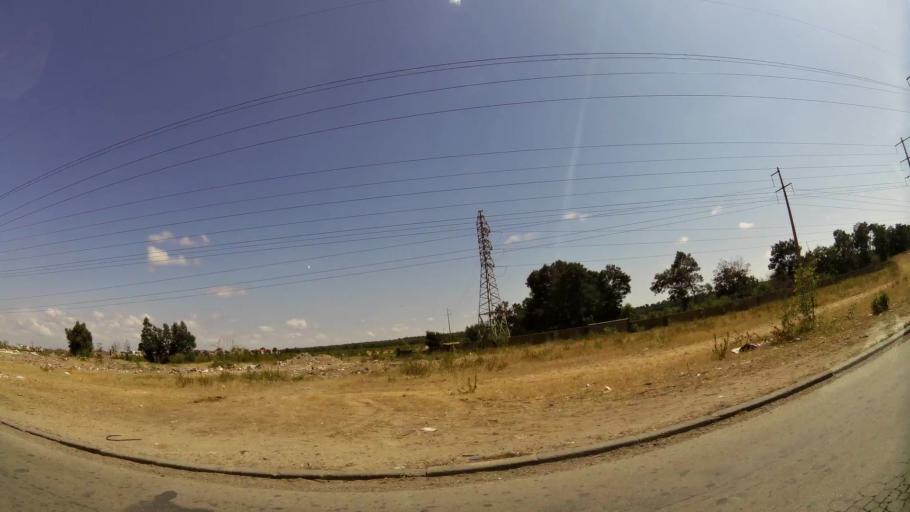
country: MA
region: Gharb-Chrarda-Beni Hssen
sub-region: Kenitra Province
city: Kenitra
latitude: 34.2371
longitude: -6.5582
